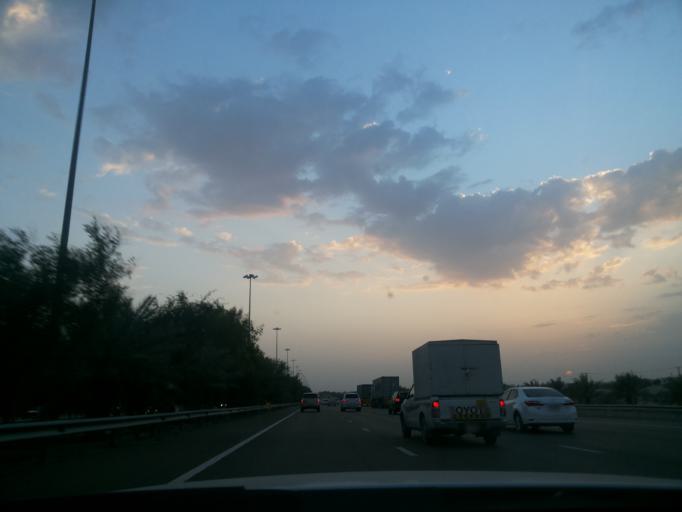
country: AE
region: Abu Dhabi
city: Abu Dhabi
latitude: 24.6461
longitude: 54.7396
